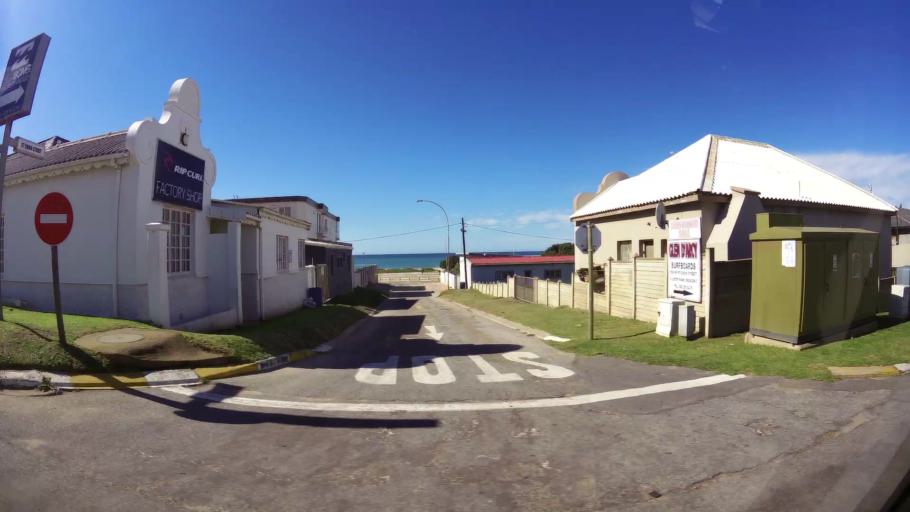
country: ZA
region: Eastern Cape
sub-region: Cacadu District Municipality
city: Jeffrey's Bay
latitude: -34.0561
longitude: 24.9225
